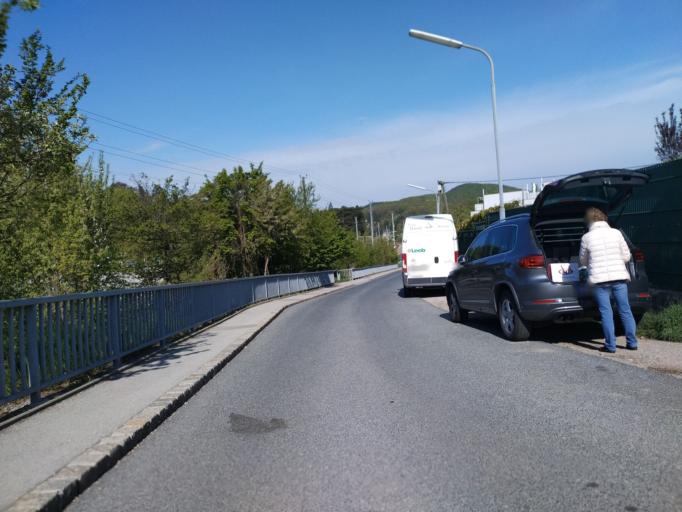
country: AT
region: Lower Austria
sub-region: Politischer Bezirk Wien-Umgebung
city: Purkersdorf
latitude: 48.2086
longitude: 16.2323
